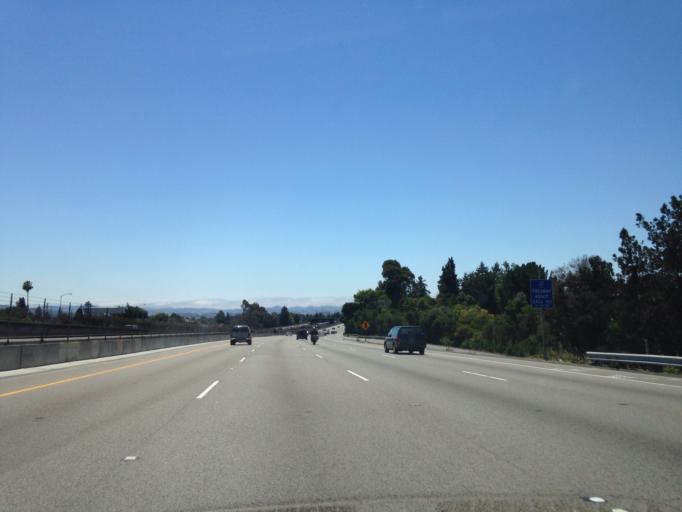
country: US
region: California
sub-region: Alameda County
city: Piedmont
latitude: 37.8476
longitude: -122.2454
